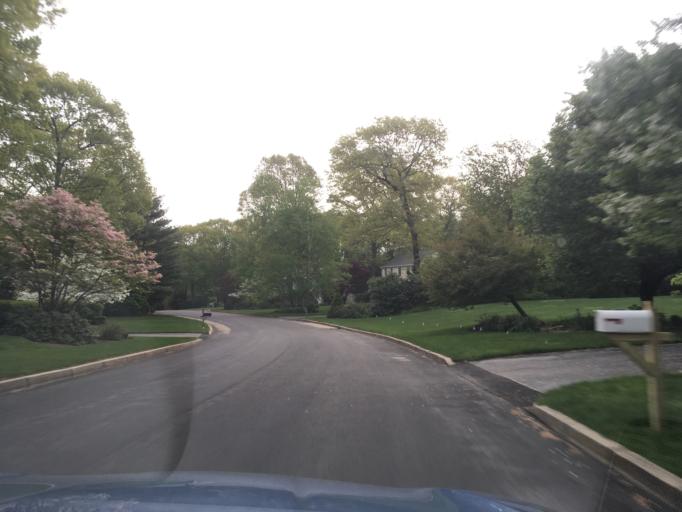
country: US
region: Rhode Island
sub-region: Kent County
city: West Warwick
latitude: 41.6600
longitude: -71.5163
